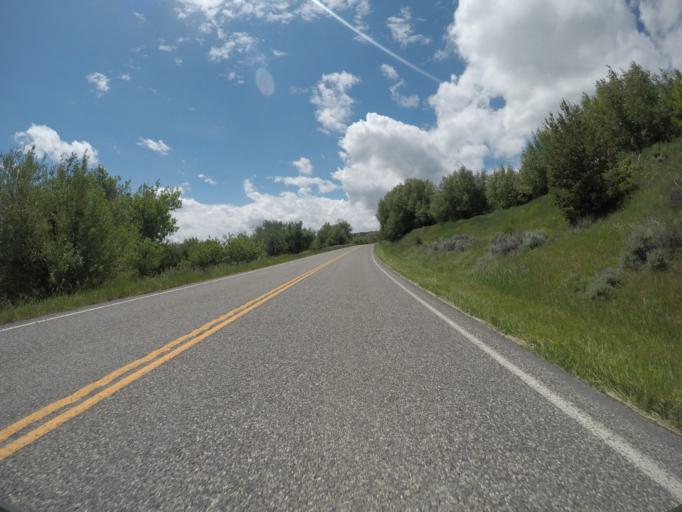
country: US
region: Montana
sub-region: Sweet Grass County
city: Big Timber
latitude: 45.6860
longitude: -110.0779
